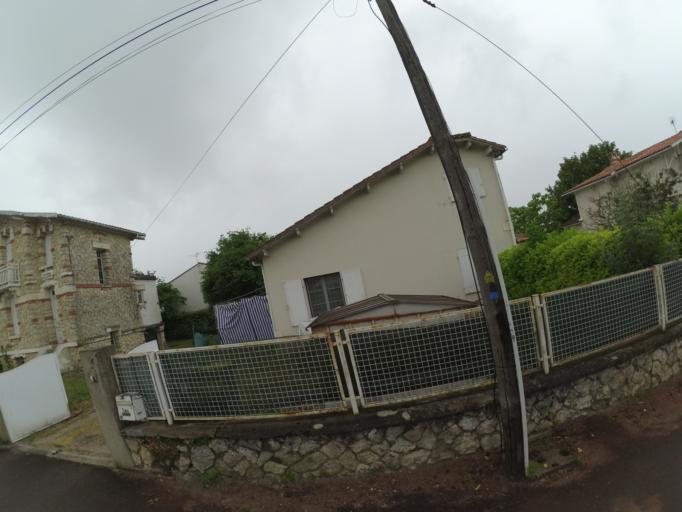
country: FR
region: Poitou-Charentes
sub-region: Departement de la Charente-Maritime
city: Royan
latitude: 45.6229
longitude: -1.0102
